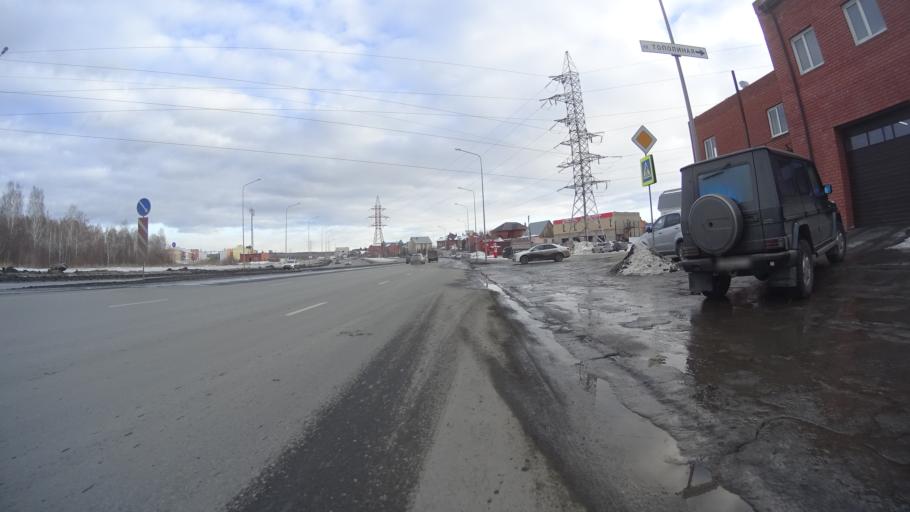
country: RU
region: Chelyabinsk
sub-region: Gorod Chelyabinsk
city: Chelyabinsk
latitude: 55.1575
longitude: 61.3061
